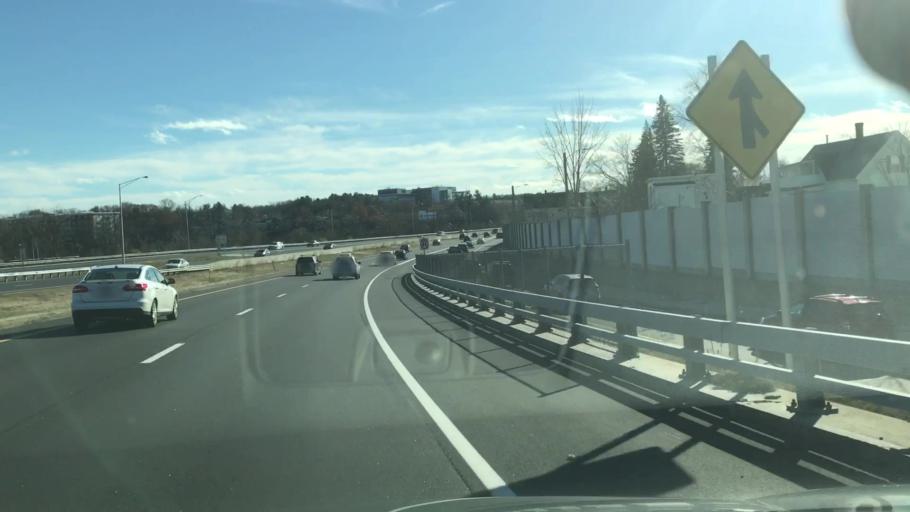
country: US
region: New Hampshire
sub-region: Hillsborough County
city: Manchester
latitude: 42.9833
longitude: -71.4708
